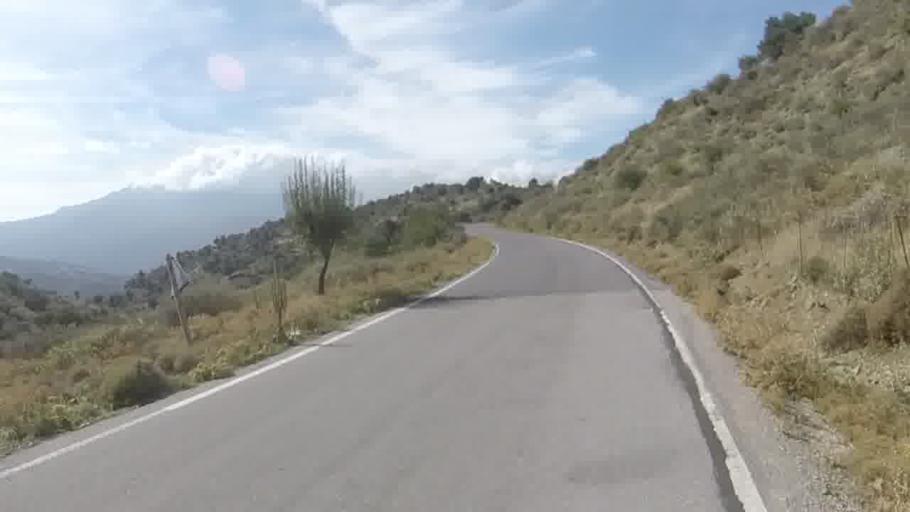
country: GR
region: Crete
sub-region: Nomos Rethymnis
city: Agia Galini
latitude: 35.1781
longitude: 24.7392
